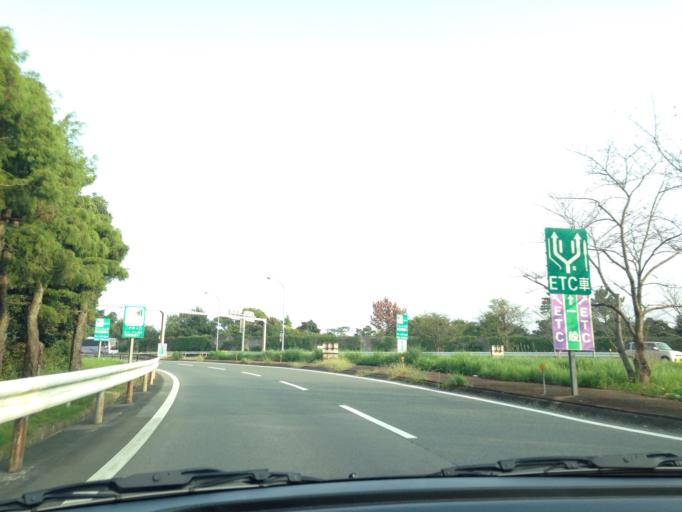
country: JP
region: Aichi
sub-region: Tokai-shi
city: Toyokawa
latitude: 34.8368
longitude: 137.4111
